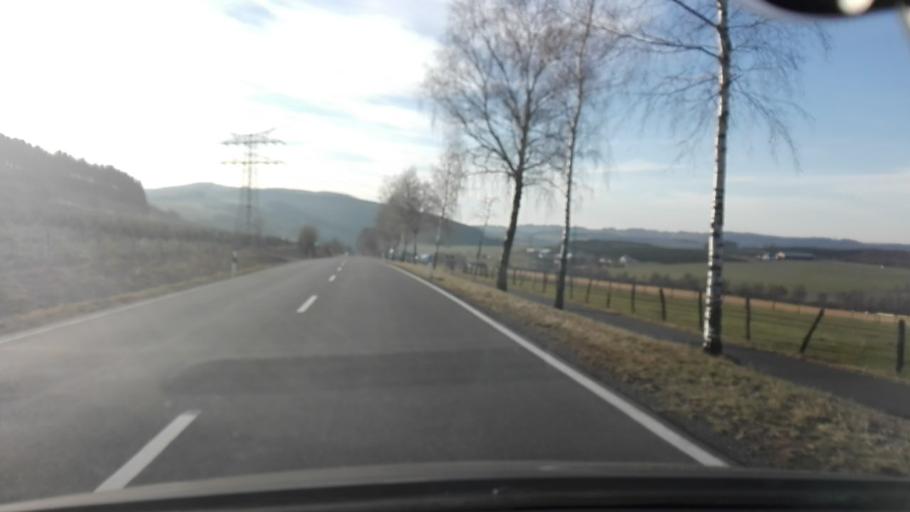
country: DE
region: North Rhine-Westphalia
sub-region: Regierungsbezirk Arnsberg
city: Schmallenberg
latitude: 51.1553
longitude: 8.2662
